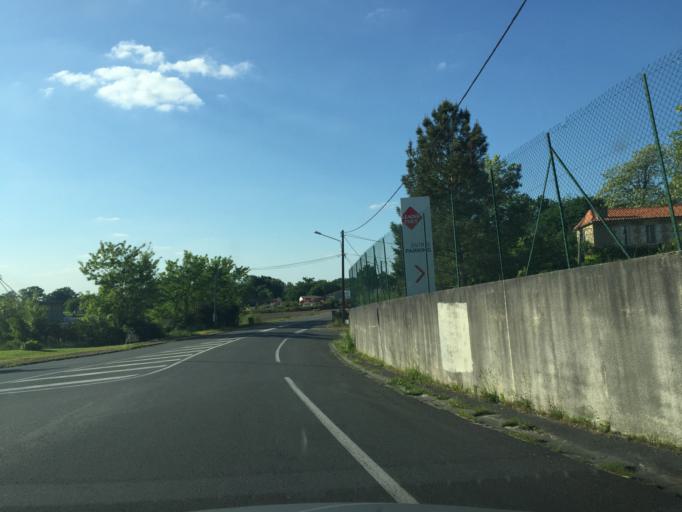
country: FR
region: Aquitaine
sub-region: Departement de la Dordogne
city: La Roche-Chalais
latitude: 45.1566
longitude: 0.0071
